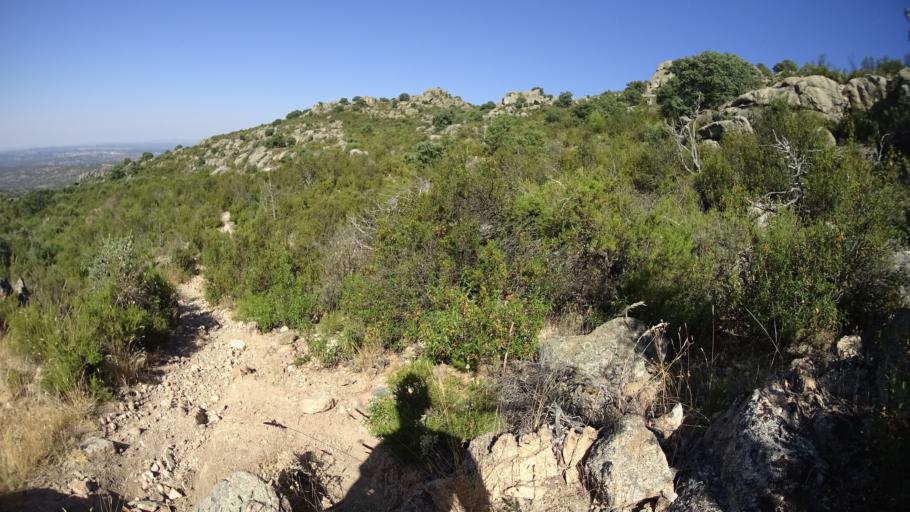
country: ES
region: Madrid
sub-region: Provincia de Madrid
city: Hoyo de Manzanares
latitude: 40.6453
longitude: -3.9350
